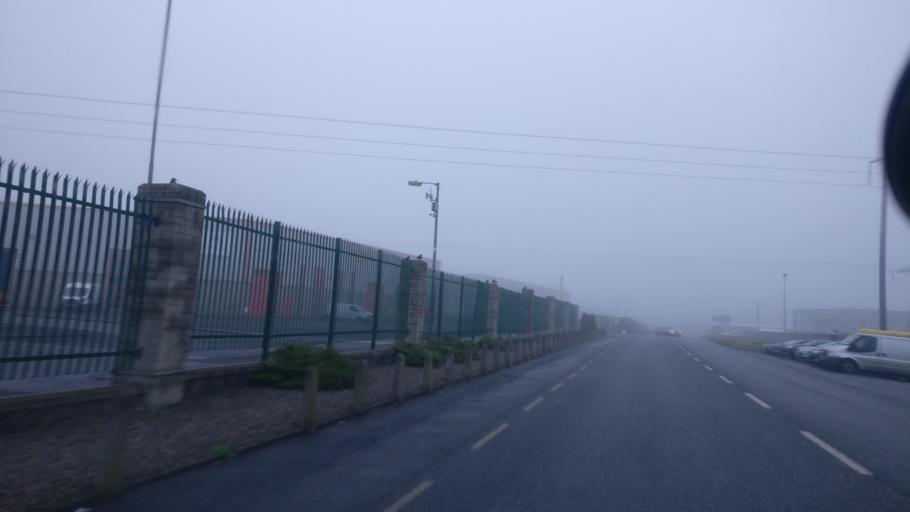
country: IE
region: Munster
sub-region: County Limerick
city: Annacotty
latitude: 52.6493
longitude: -8.5836
